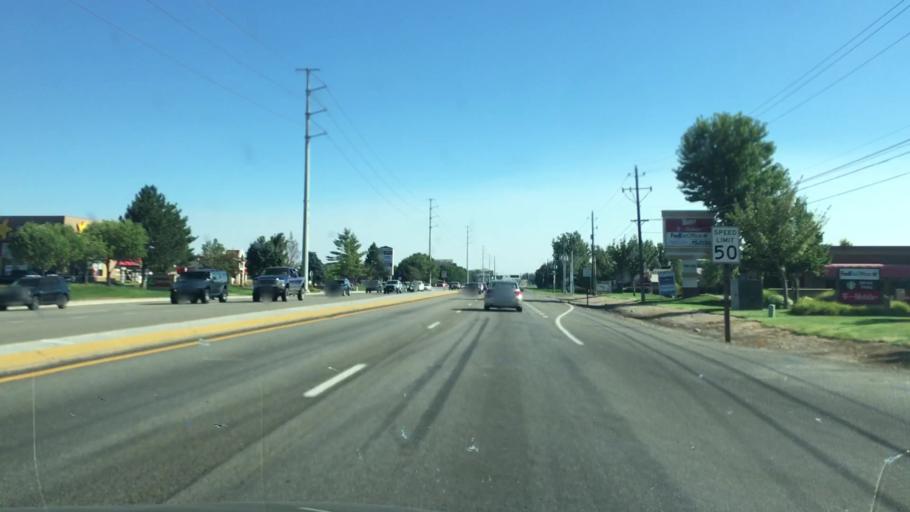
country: US
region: Idaho
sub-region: Ada County
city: Meridian
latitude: 43.6179
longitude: -116.3547
